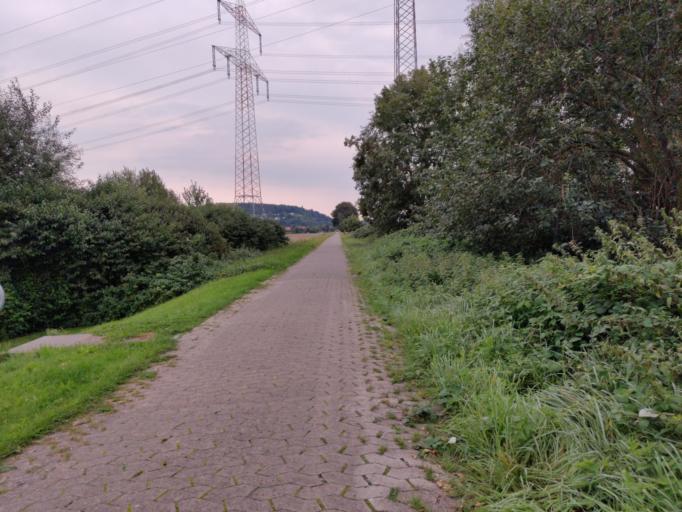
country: DE
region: Lower Saxony
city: Hameln
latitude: 52.0590
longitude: 9.3804
